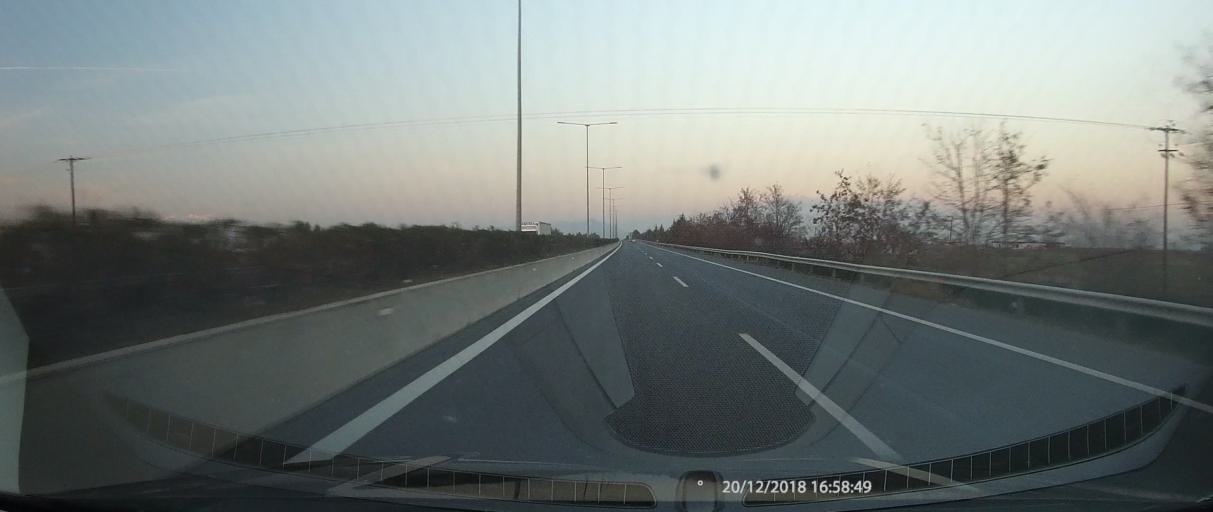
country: GR
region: Thessaly
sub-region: Nomos Larisis
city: Platykampos
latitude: 39.6017
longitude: 22.4960
